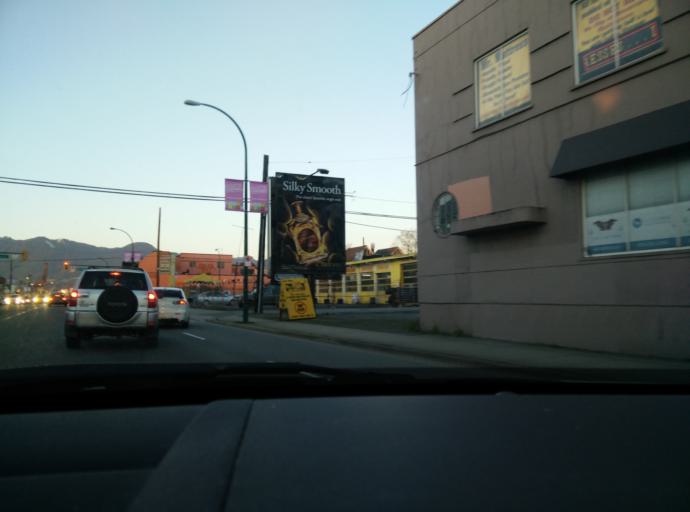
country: CA
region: British Columbia
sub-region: Fraser Valley Regional District
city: North Vancouver
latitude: 49.2768
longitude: -123.0772
